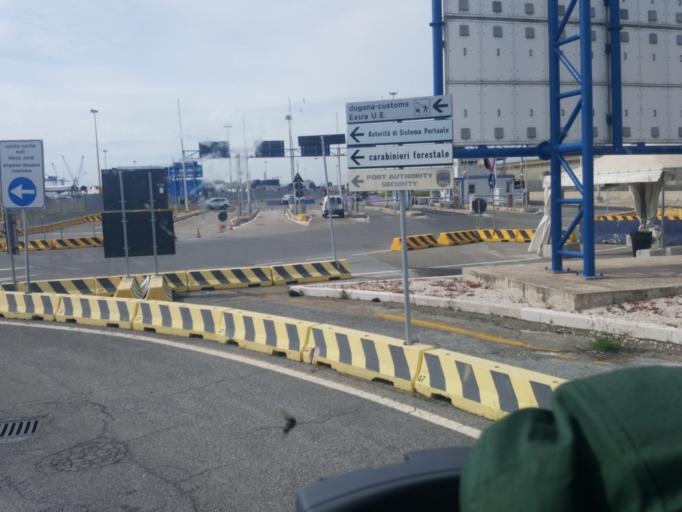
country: IT
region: Latium
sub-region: Citta metropolitana di Roma Capitale
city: Civitavecchia
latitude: 42.0966
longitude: 11.7867
